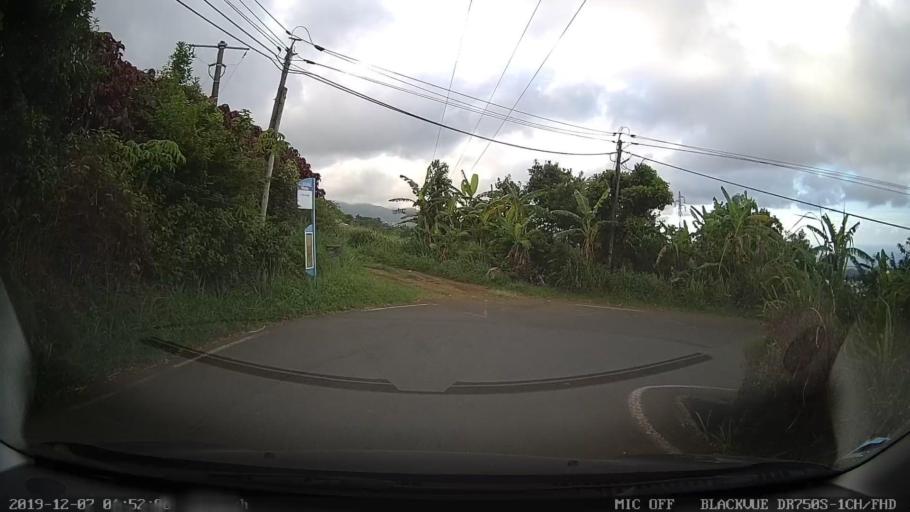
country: RE
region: Reunion
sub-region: Reunion
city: Sainte-Marie
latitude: -20.9402
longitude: 55.5341
